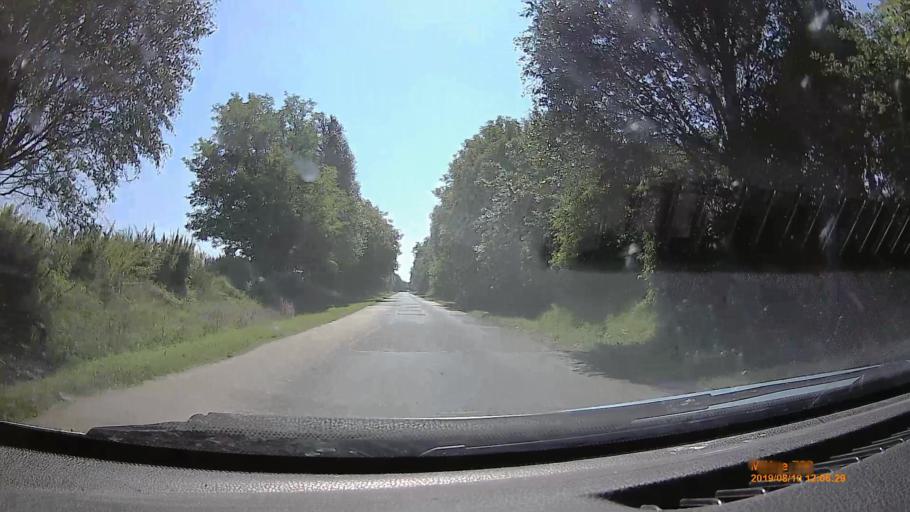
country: HU
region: Somogy
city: Somogyvar
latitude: 46.5785
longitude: 17.6757
